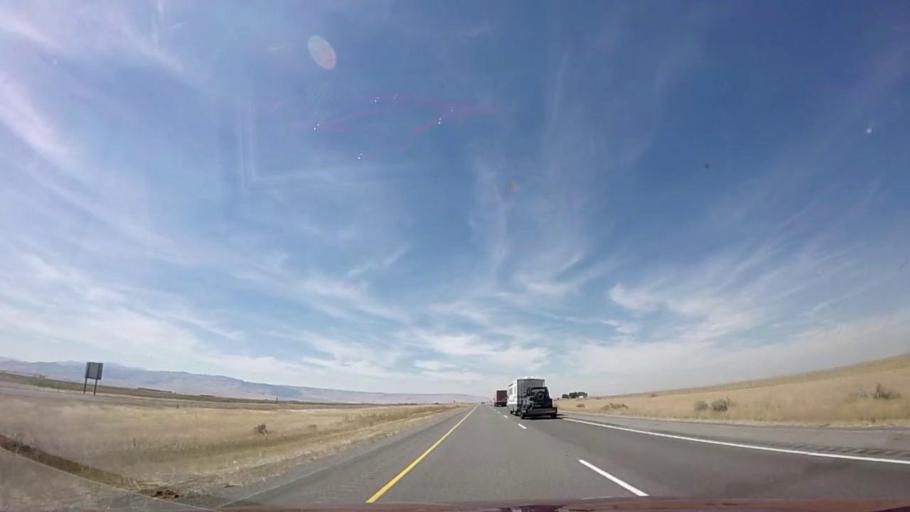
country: US
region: Idaho
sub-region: Minidoka County
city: Rupert
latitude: 42.3351
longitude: -113.2230
